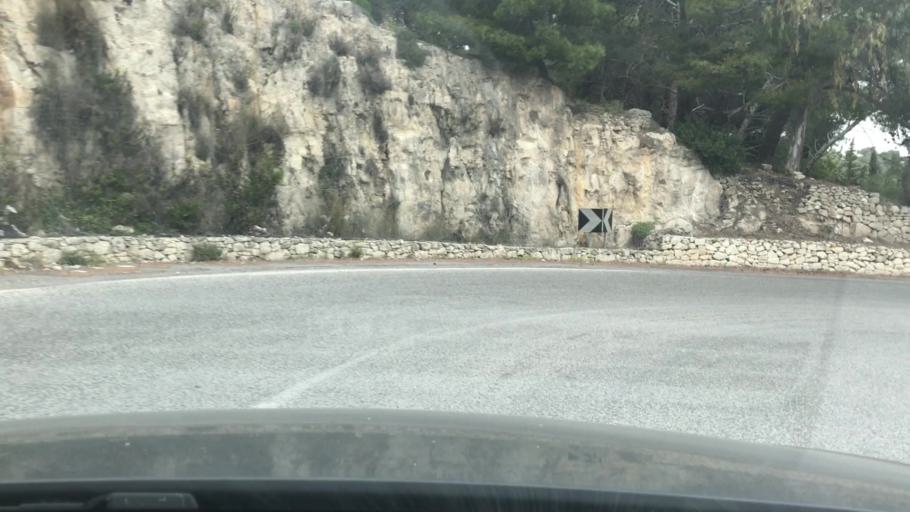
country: IT
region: Sicily
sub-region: Ragusa
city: Scicli
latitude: 36.7960
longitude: 14.7109
